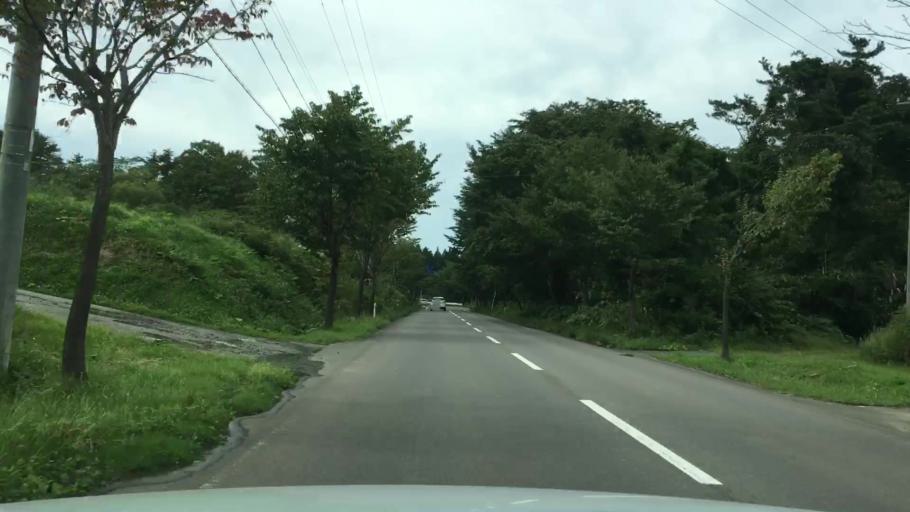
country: JP
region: Aomori
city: Shimokizukuri
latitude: 40.7115
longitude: 140.2830
